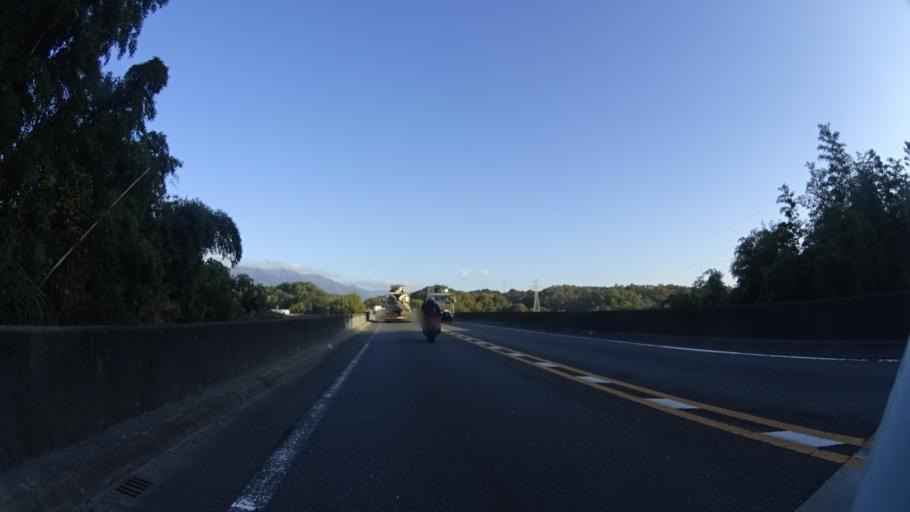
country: JP
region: Shiga Prefecture
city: Kitahama
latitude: 35.1153
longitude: 135.8980
